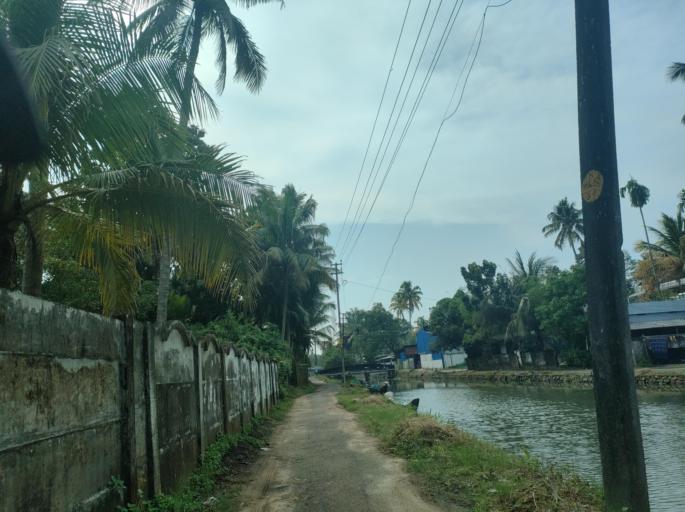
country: IN
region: Kerala
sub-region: Ernakulam
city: Elur
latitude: 10.0809
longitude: 76.2130
